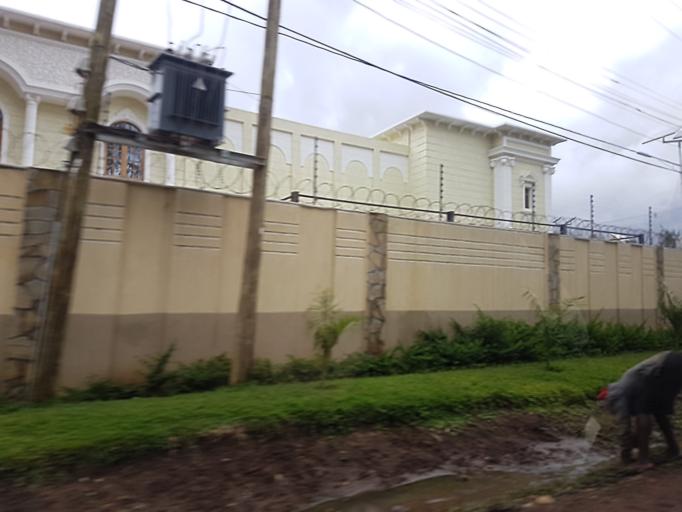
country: KE
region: Kajiado
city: Ngong
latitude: -1.3557
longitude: 36.7282
